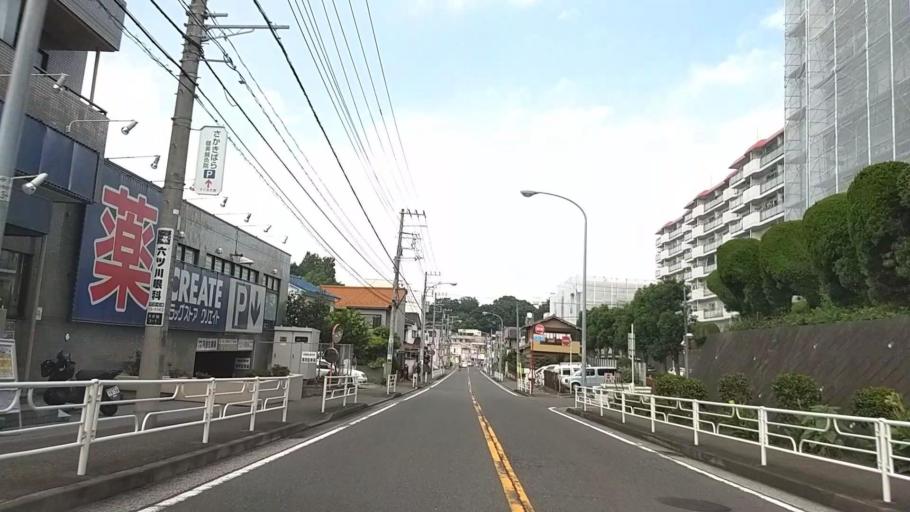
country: JP
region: Kanagawa
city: Yokohama
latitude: 35.4148
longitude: 139.5764
